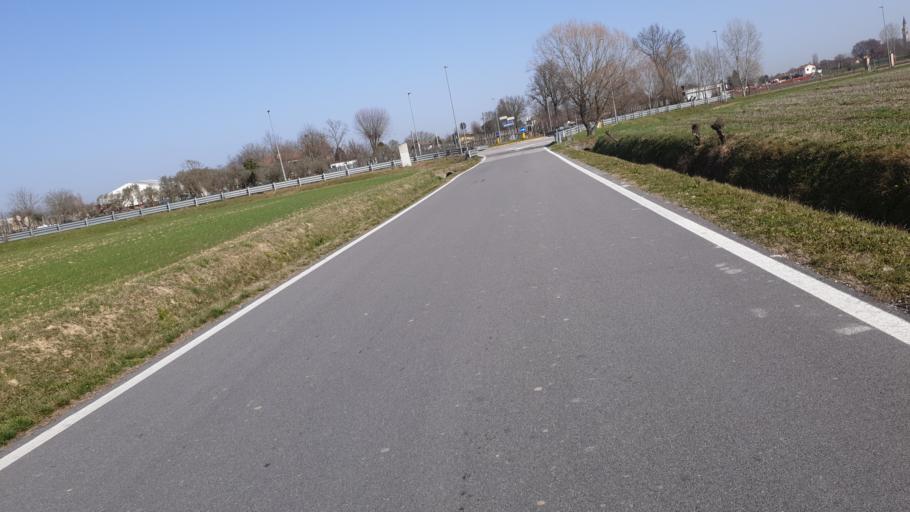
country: IT
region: Veneto
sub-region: Provincia di Padova
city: Cavino
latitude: 45.4942
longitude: 11.8937
